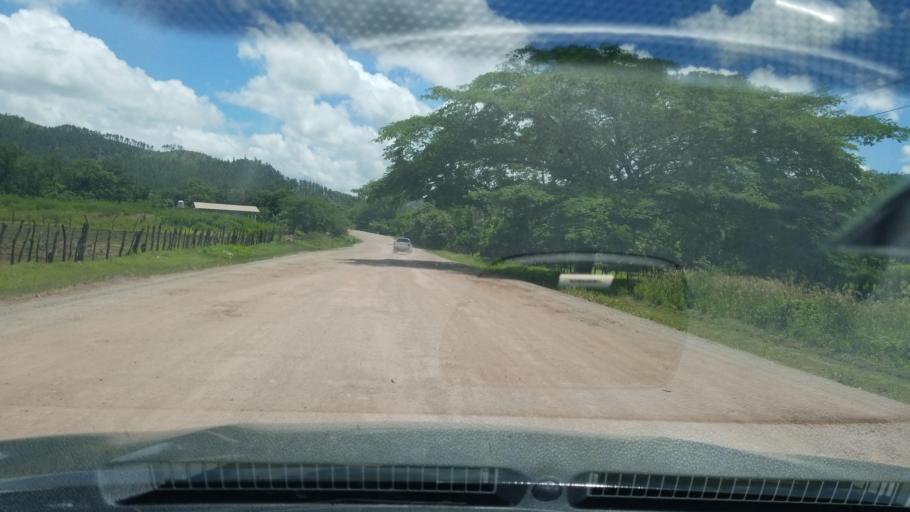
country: HN
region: Francisco Morazan
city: San Juan de Flores
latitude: 14.3279
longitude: -87.0463
